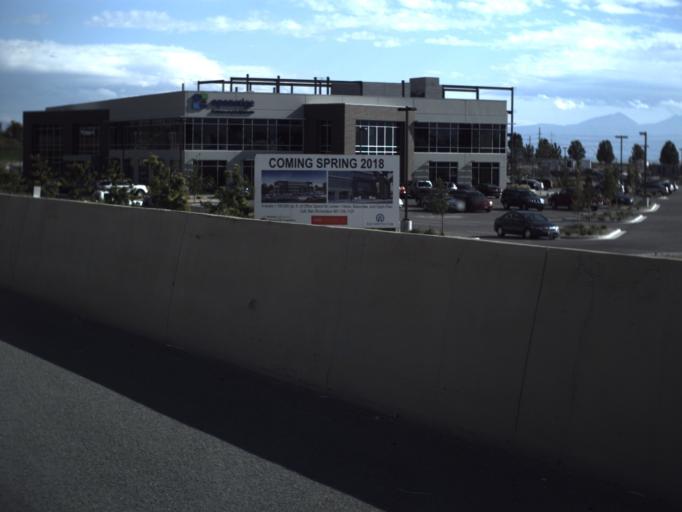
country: US
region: Utah
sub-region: Utah County
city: American Fork
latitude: 40.3513
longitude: -111.7719
